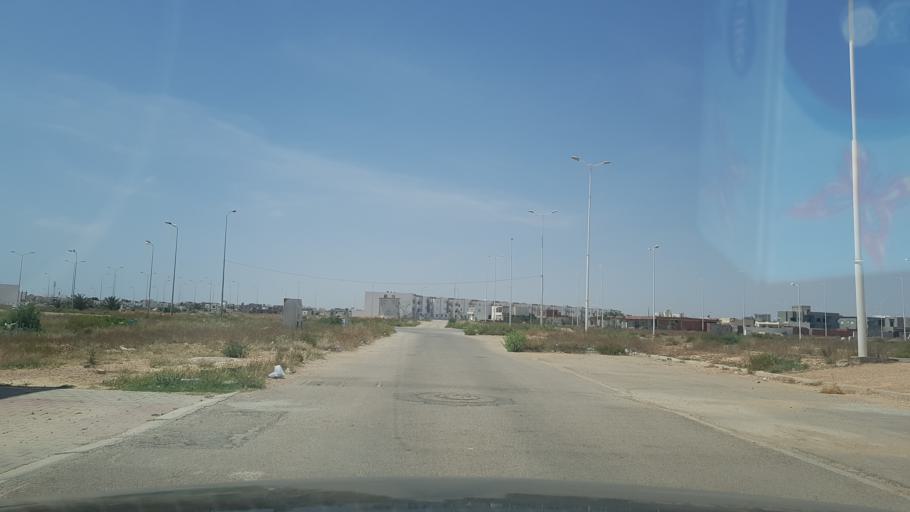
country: TN
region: Safaqis
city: Al Qarmadah
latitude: 34.8330
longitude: 10.7564
